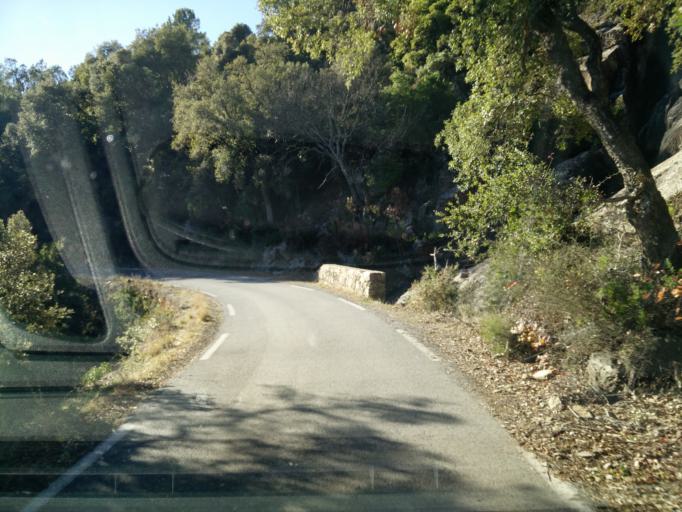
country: FR
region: Provence-Alpes-Cote d'Azur
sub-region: Departement du Var
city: Collobrieres
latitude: 43.2511
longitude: 6.3858
